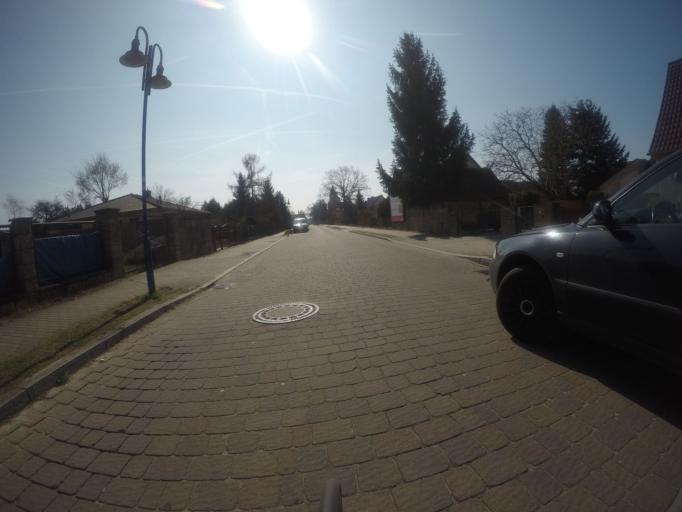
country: DE
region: Brandenburg
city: Erkner
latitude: 52.3962
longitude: 13.7128
